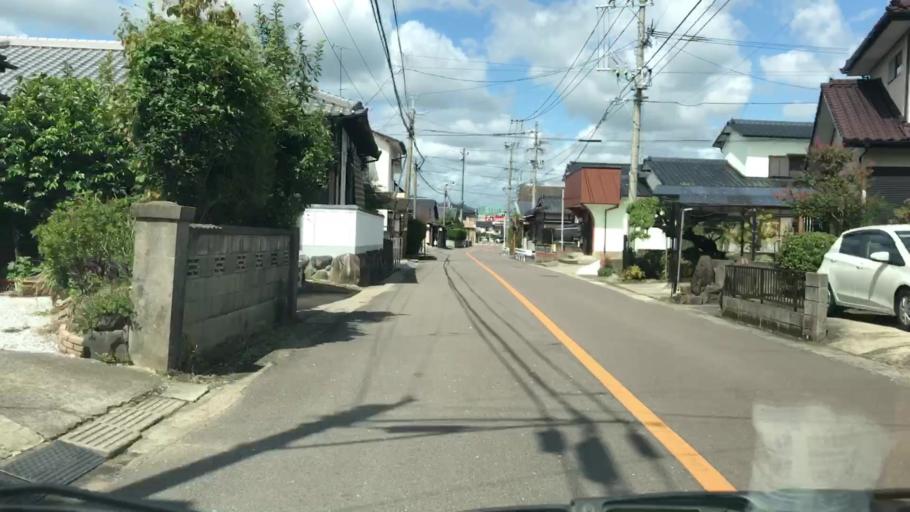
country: JP
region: Saga Prefecture
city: Saga-shi
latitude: 33.2447
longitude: 130.2028
